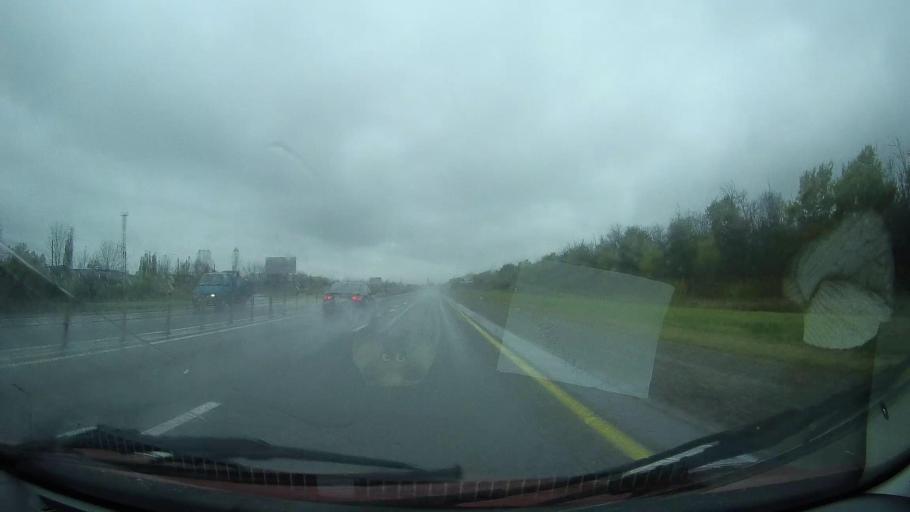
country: RU
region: Stavropol'skiy
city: Nevinnomyssk
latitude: 44.6405
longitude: 41.9698
